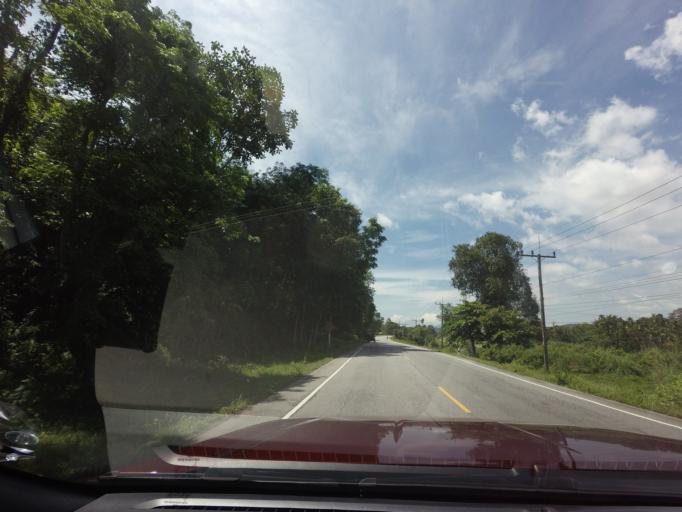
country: TH
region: Narathiwat
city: Yi-ngo
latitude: 6.3540
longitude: 101.6166
